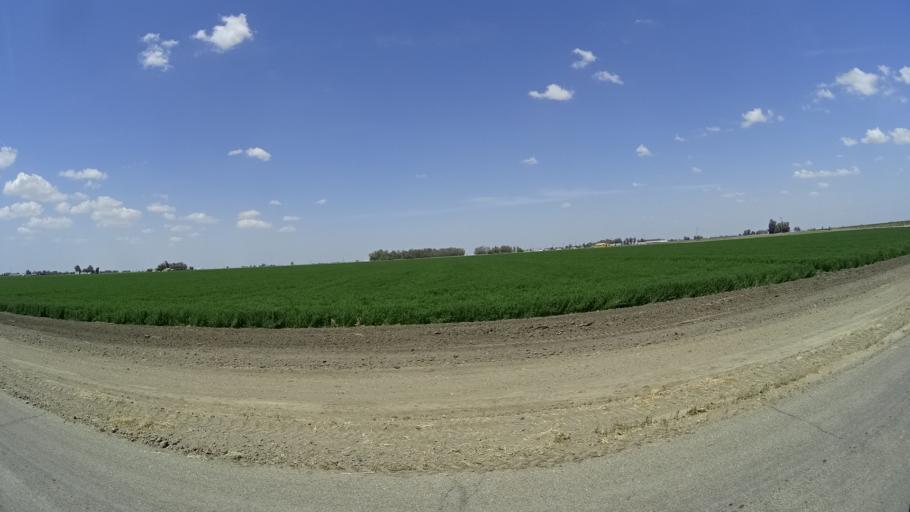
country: US
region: California
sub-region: Kings County
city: Stratford
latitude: 36.1823
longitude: -119.8003
